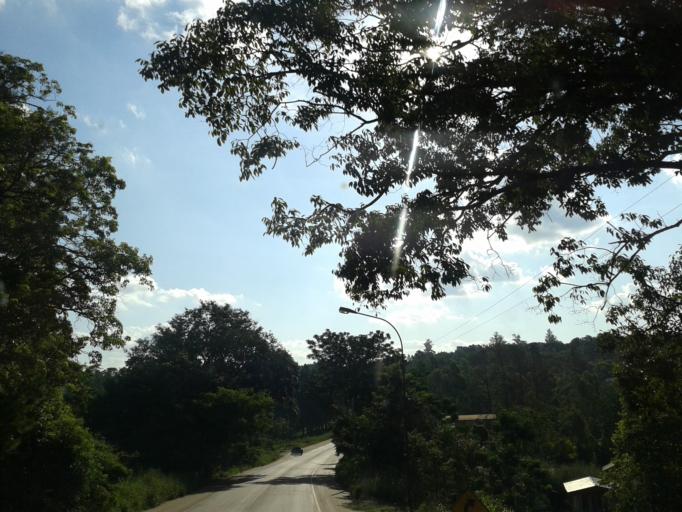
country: AR
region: Misiones
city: Guarani
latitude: -27.4942
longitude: -55.1631
